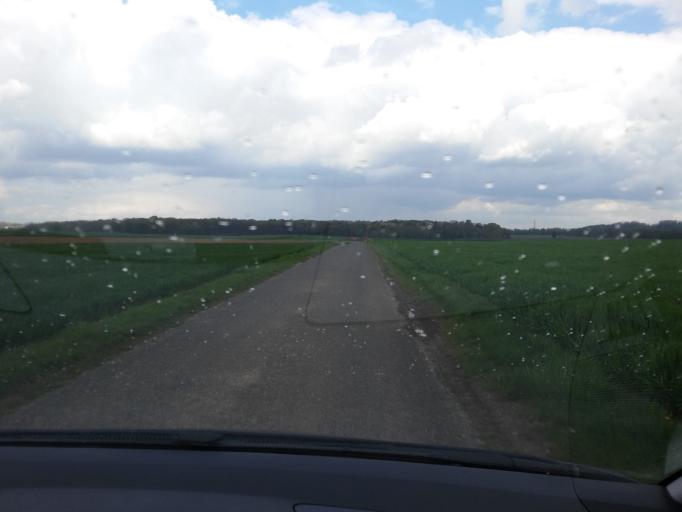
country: FR
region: Picardie
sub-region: Departement de l'Oise
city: Chevrieres
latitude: 49.3685
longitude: 2.6858
